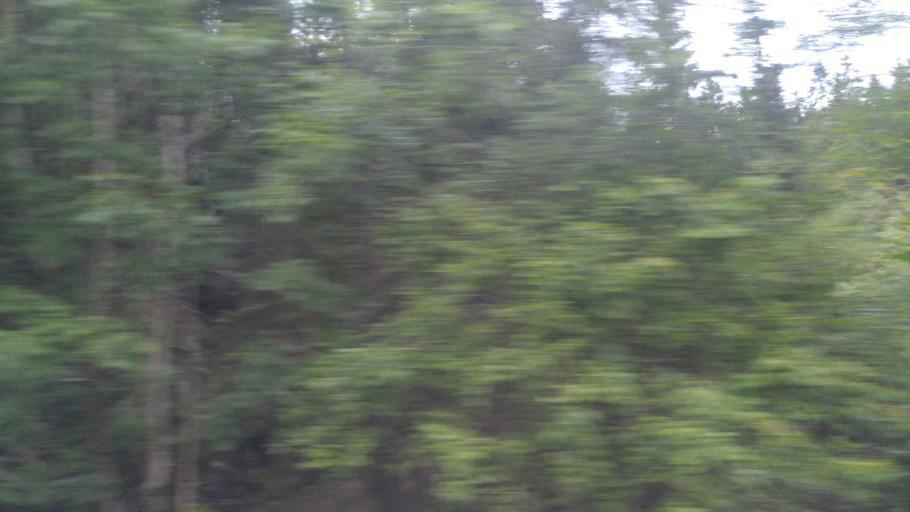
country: NO
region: Oslo
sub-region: Oslo
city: Sjolyststranda
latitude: 59.9623
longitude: 10.6885
